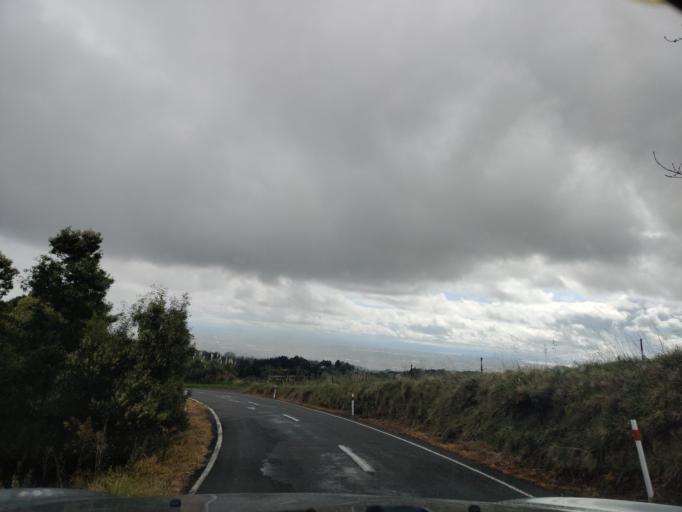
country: NZ
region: Hawke's Bay
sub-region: Hastings District
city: Hastings
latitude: -39.6932
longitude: 176.9019
